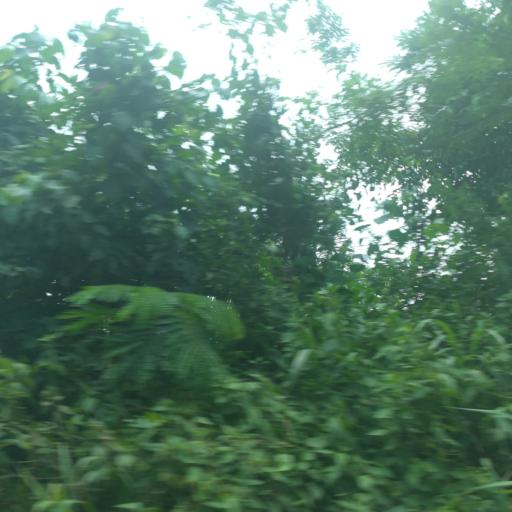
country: NG
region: Lagos
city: Ejirin
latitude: 6.6741
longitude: 3.8003
